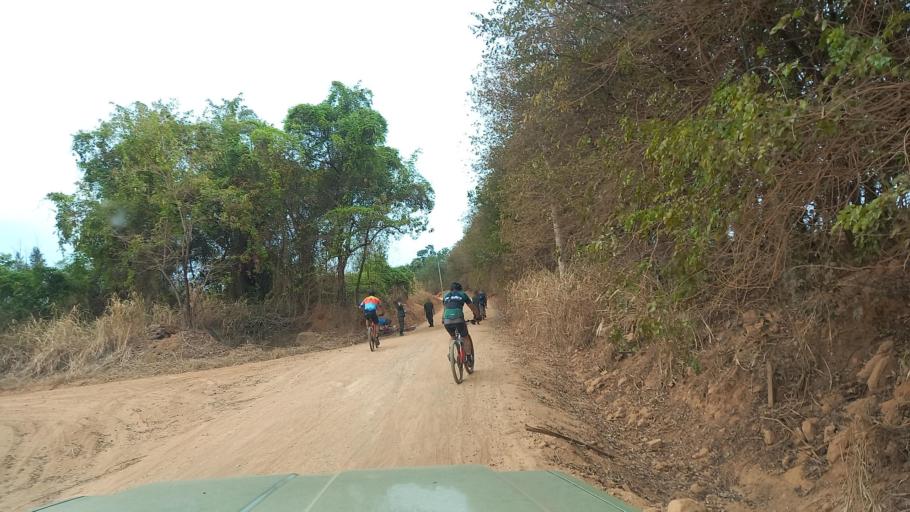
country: BR
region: Sao Paulo
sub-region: Moji-Guacu
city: Mogi-Gaucu
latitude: -22.2868
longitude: -46.8444
